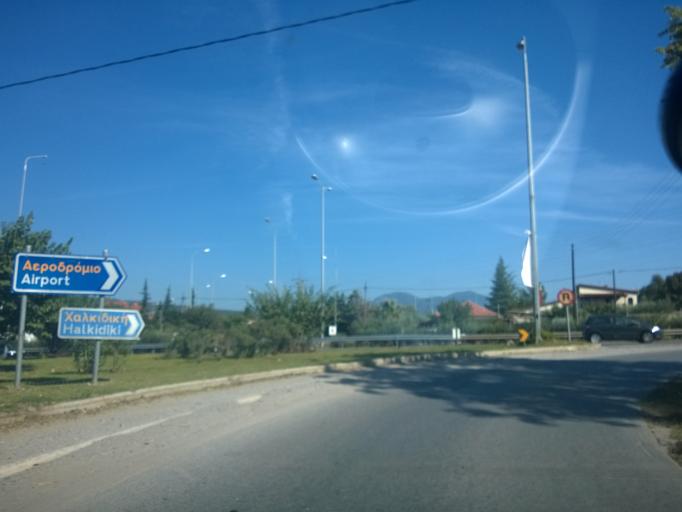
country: GR
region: Central Macedonia
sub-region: Nomos Thessalonikis
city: Pylaia
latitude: 40.6006
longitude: 22.9975
